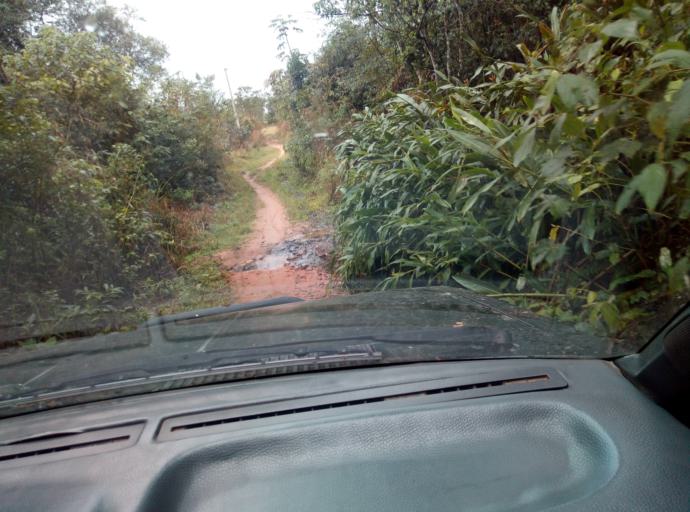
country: PY
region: Caaguazu
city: Carayao
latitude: -25.1965
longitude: -56.3544
